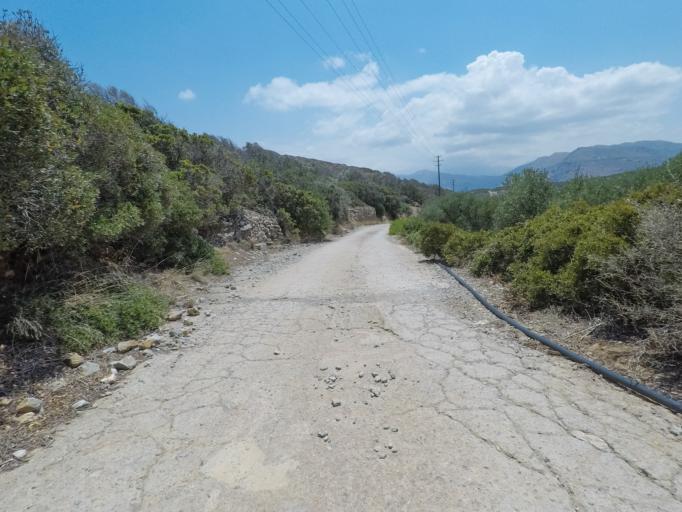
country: GR
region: Crete
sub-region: Nomos Lasithiou
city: Elounda
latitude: 35.3199
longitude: 25.7498
